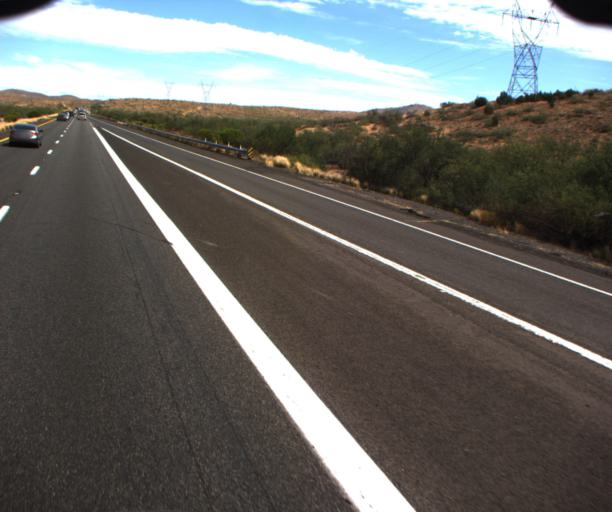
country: US
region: Arizona
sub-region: Yavapai County
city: Cordes Lakes
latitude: 34.2404
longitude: -112.1117
